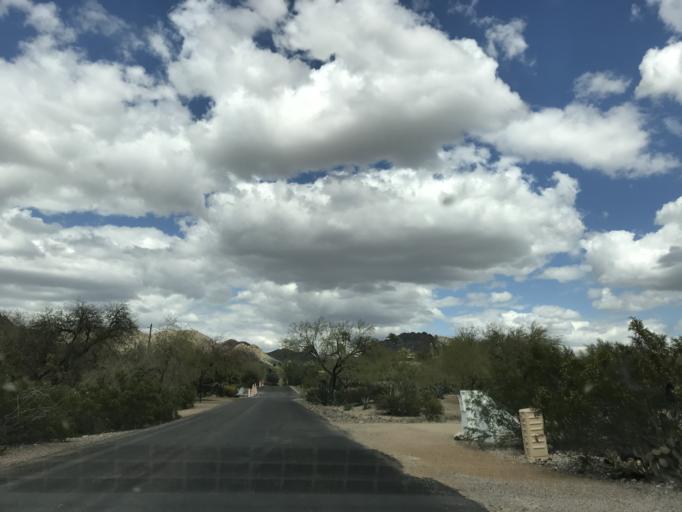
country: US
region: Arizona
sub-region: Maricopa County
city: Paradise Valley
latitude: 33.5205
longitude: -112.0067
